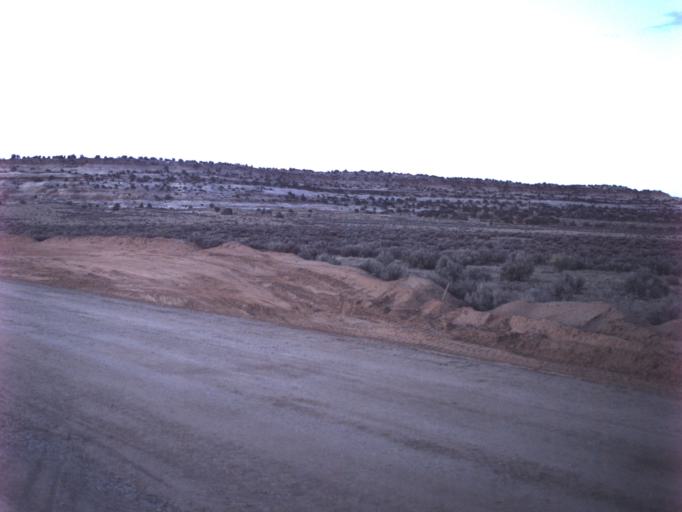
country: US
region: Utah
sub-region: San Juan County
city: Monticello
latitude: 38.0926
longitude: -109.3575
